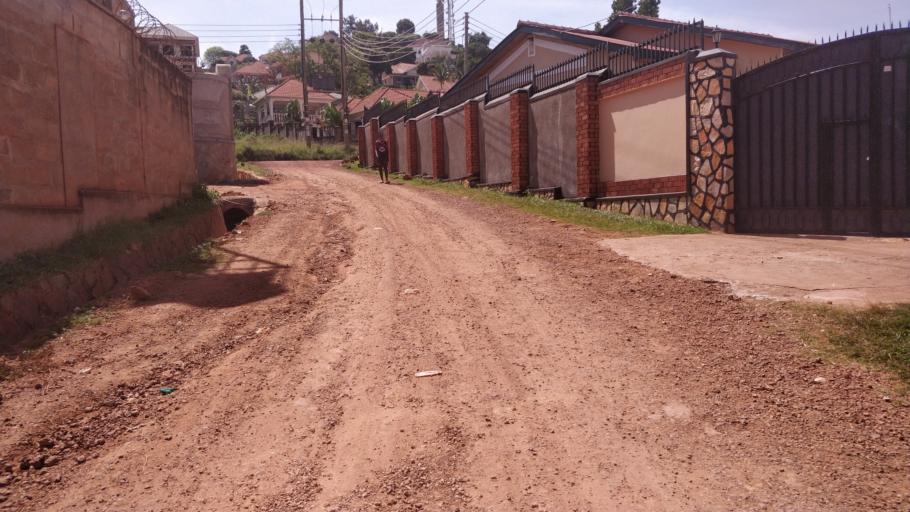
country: UG
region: Central Region
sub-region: Kampala District
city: Kampala
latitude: 0.2677
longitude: 32.6101
